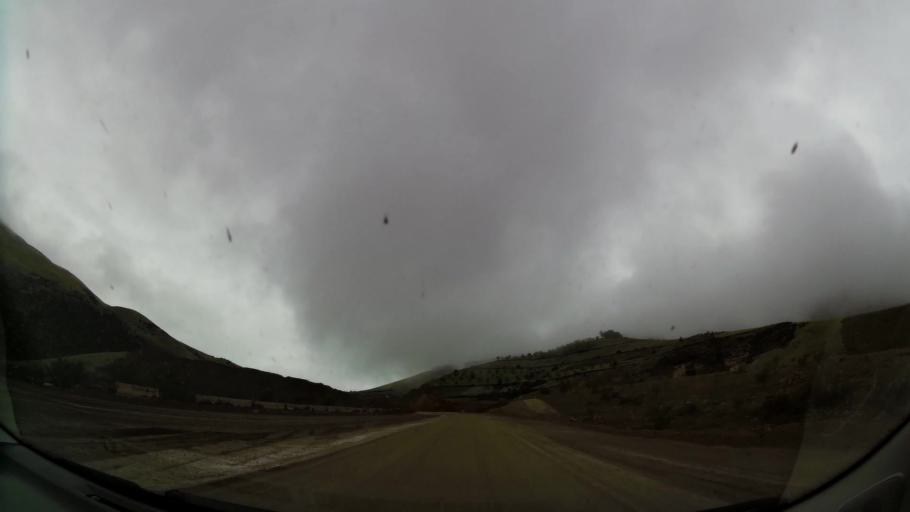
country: MA
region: Taza-Al Hoceima-Taounate
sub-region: Taza
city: Ajdir
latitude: 34.9105
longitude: -3.7965
